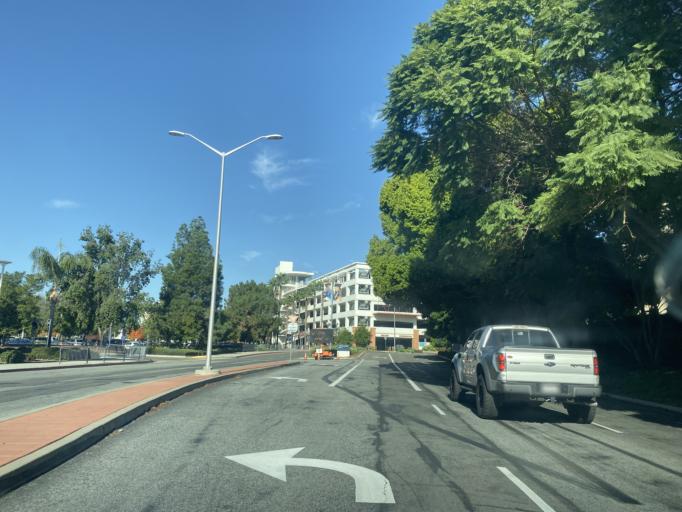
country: US
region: California
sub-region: Orange County
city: Placentia
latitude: 33.8790
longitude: -117.8826
